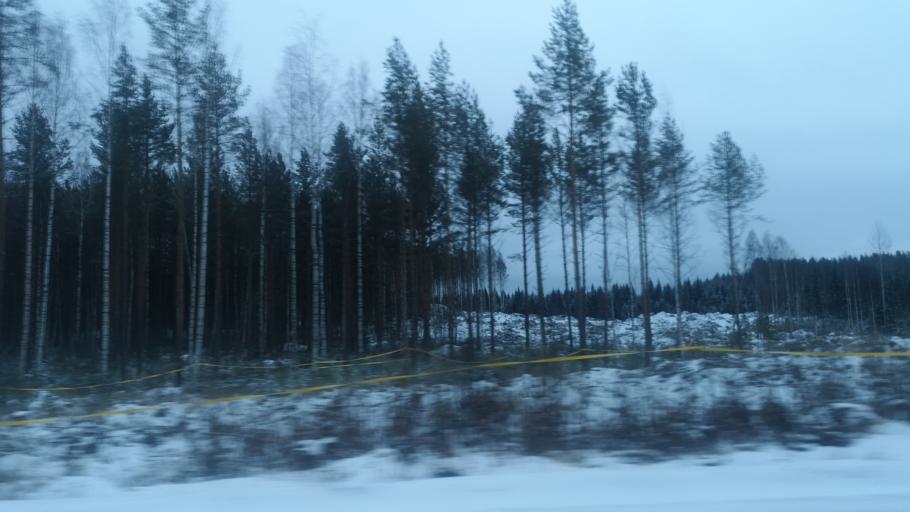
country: FI
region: Southern Savonia
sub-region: Savonlinna
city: Enonkoski
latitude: 62.0926
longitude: 28.6715
